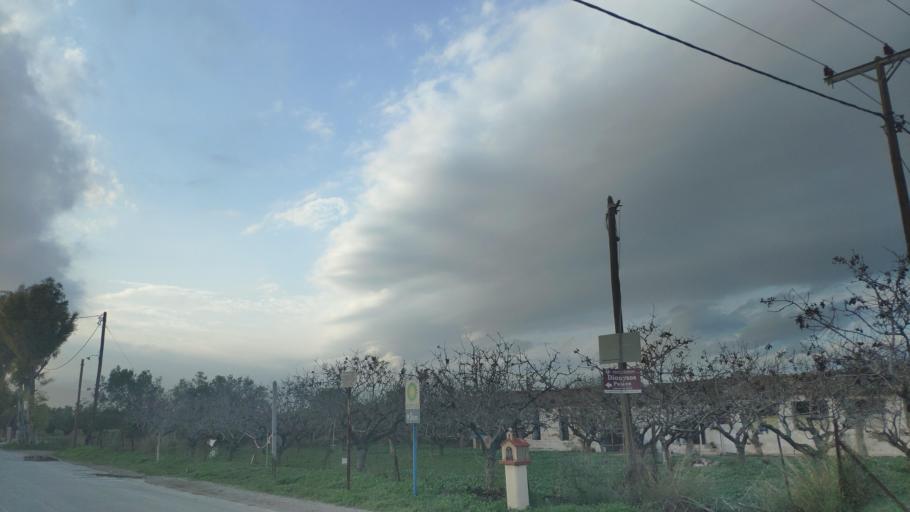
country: GR
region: Attica
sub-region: Nomarchia Dytikis Attikis
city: Nea Peramos
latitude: 37.9998
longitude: 23.3864
